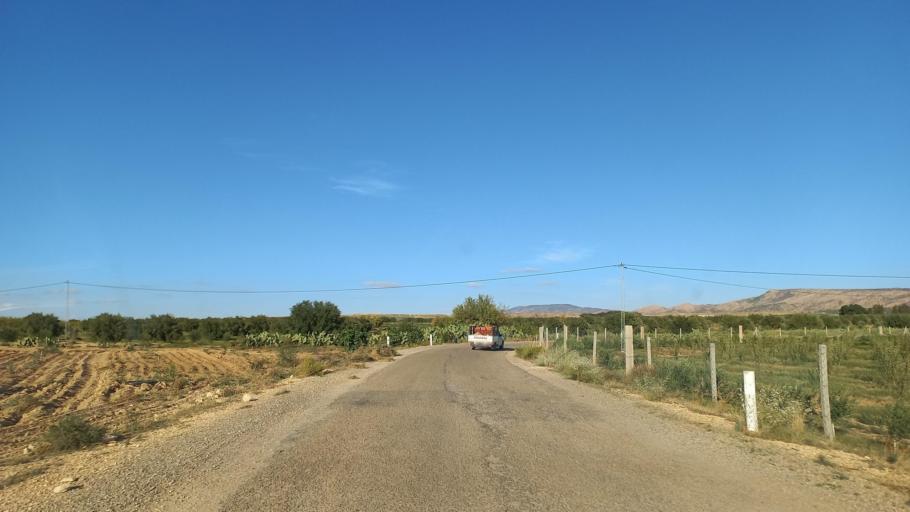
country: TN
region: Al Qasrayn
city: Sbiba
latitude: 35.3343
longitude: 9.0912
